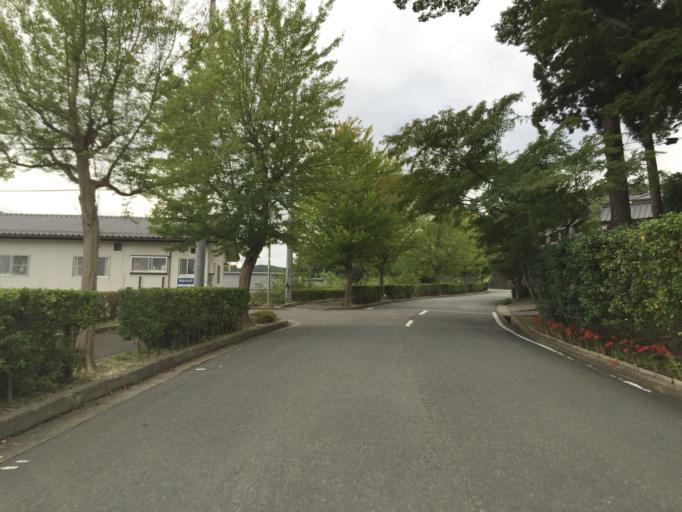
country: JP
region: Fukushima
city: Fukushima-shi
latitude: 37.7685
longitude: 140.4941
